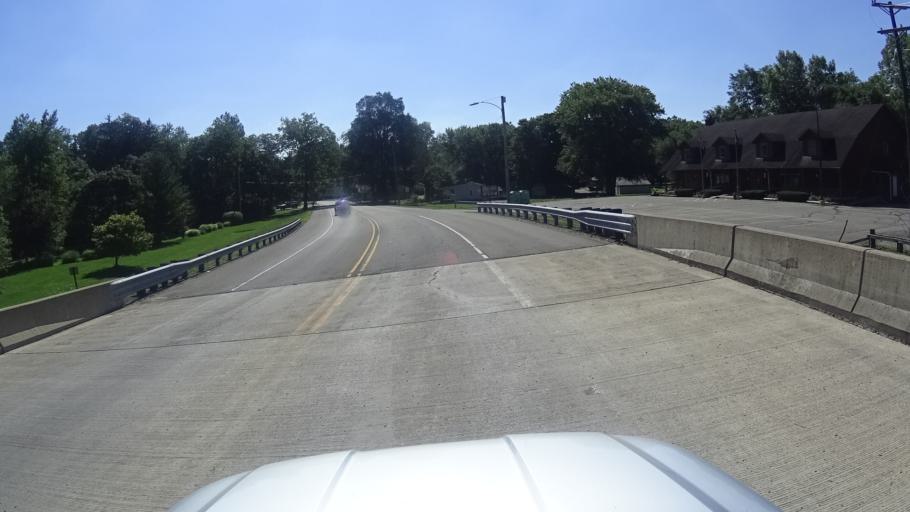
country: US
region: Indiana
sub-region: Madison County
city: Pendleton
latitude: 40.0024
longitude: -85.7553
